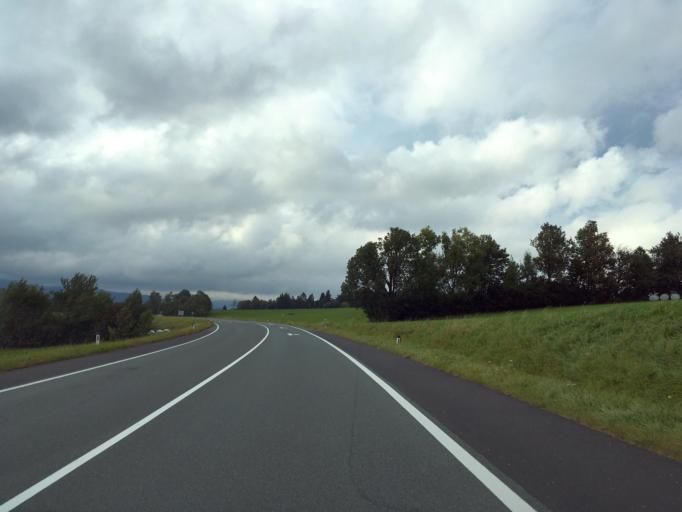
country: AT
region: Styria
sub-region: Politischer Bezirk Hartberg-Fuerstenfeld
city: Pinggau
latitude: 47.4546
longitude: 16.0716
